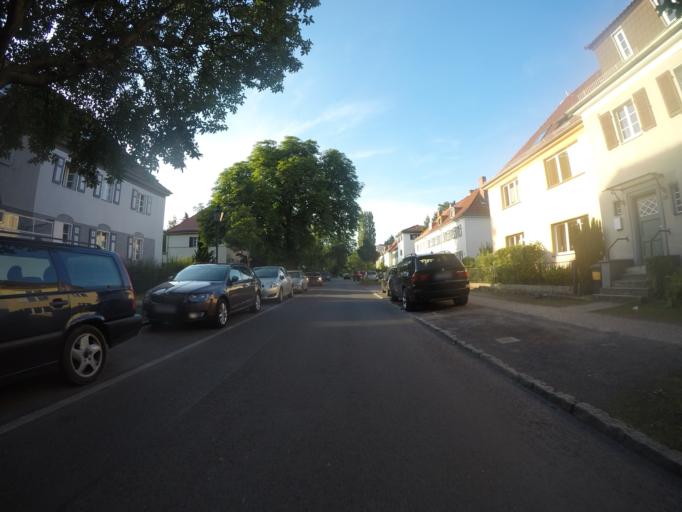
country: DE
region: Berlin
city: Grunewald
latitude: 52.5029
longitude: 13.2591
